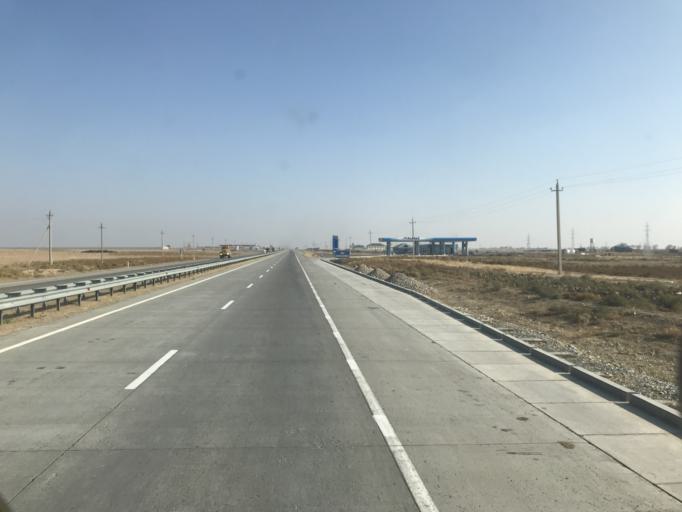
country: KZ
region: Ongtustik Qazaqstan
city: Shymkent
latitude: 42.4560
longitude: 69.6063
